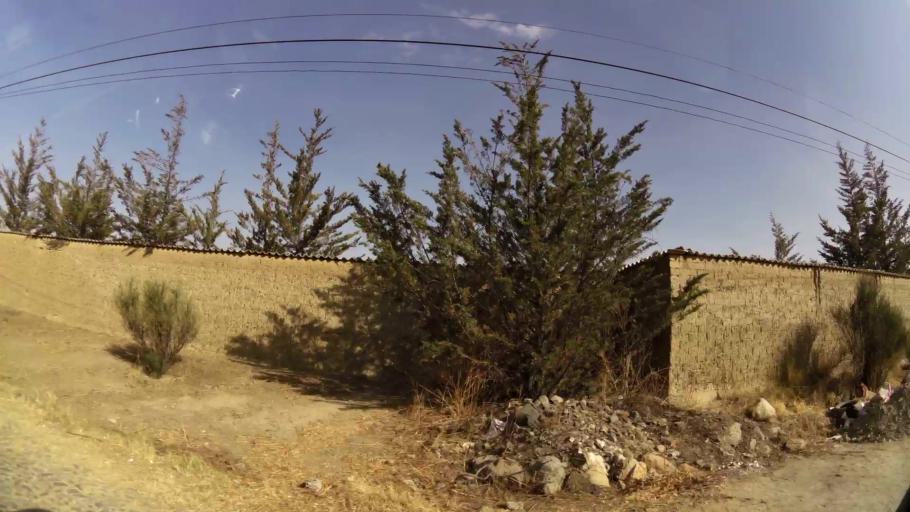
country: BO
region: La Paz
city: La Paz
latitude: -16.5284
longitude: -68.0801
